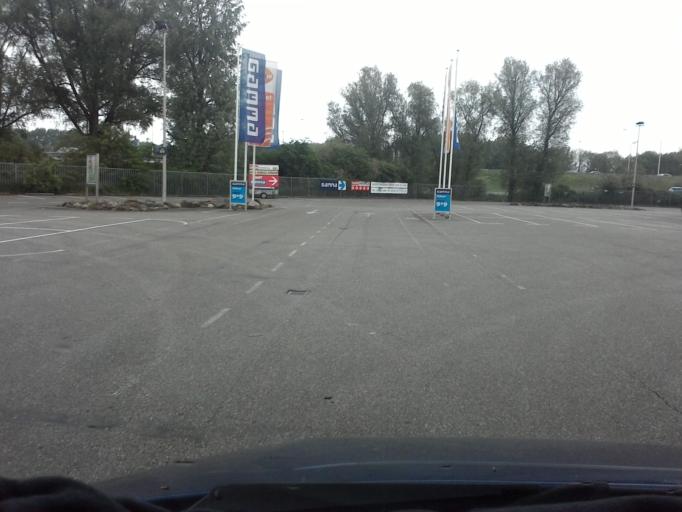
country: NL
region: Utrecht
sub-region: Gemeente Utrecht
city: Lunetten
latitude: 52.0546
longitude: 5.1238
